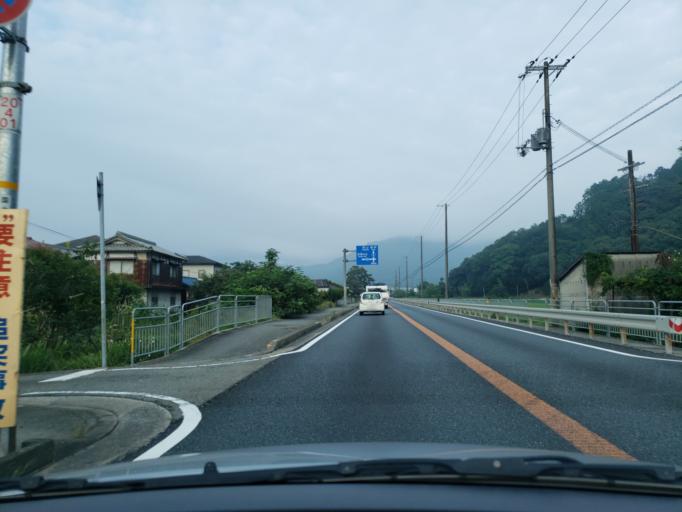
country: JP
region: Hyogo
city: Kariya
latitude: 34.8263
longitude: 134.3765
